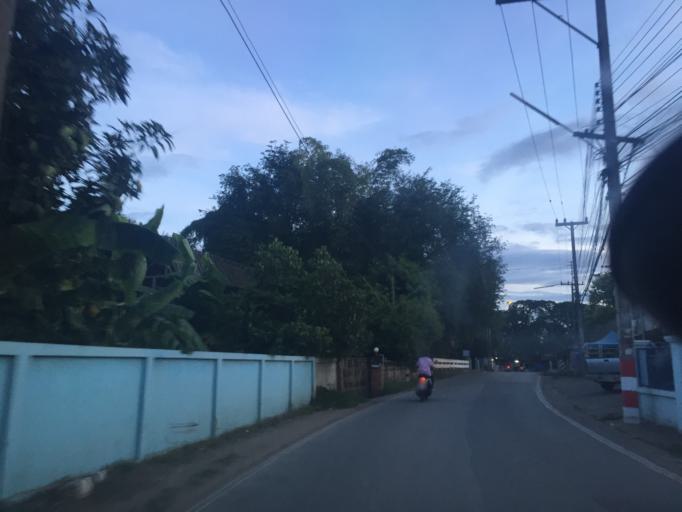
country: TH
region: Lamphun
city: Lamphun
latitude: 18.5542
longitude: 99.0358
